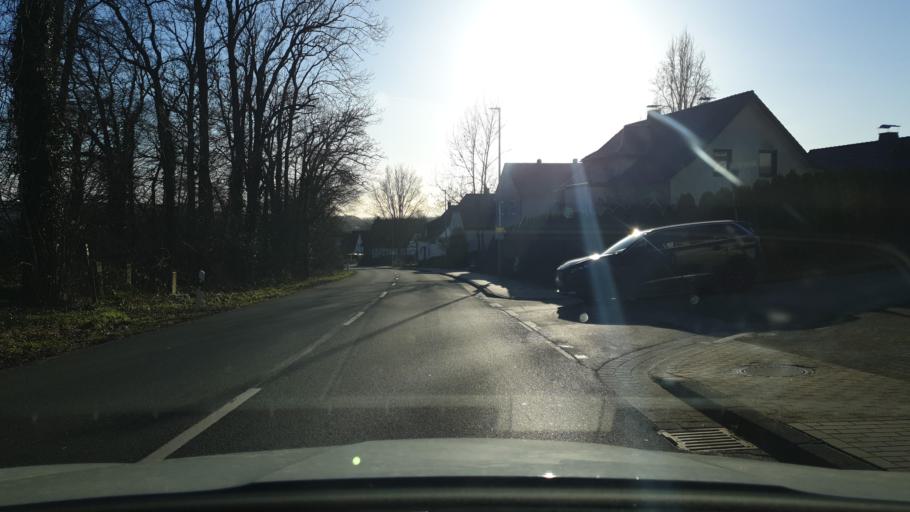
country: DE
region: North Rhine-Westphalia
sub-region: Regierungsbezirk Detmold
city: Kirchlengern
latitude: 52.2008
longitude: 8.6468
